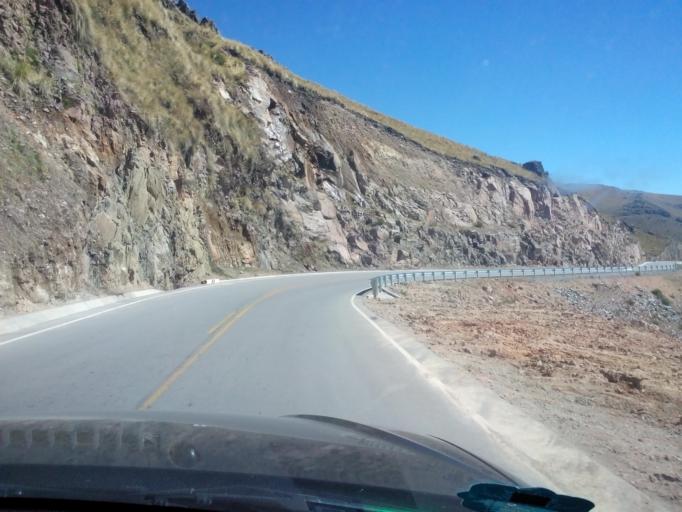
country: PE
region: Ayacucho
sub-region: Provincia de Huamanga
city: Ocros
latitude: -13.3928
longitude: -73.9514
